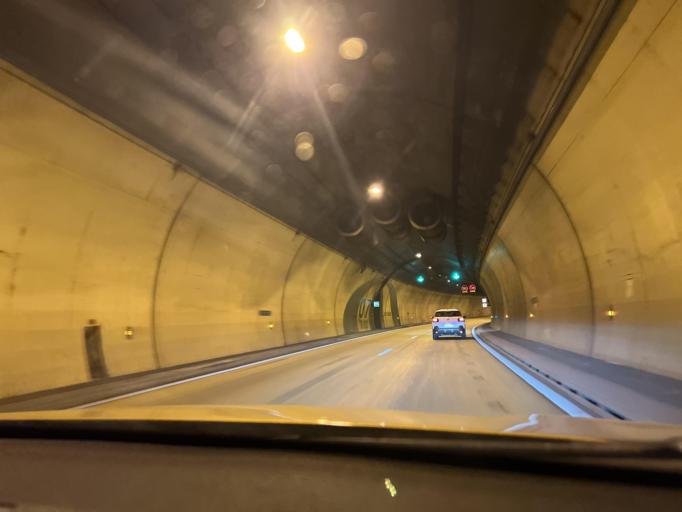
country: FR
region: Provence-Alpes-Cote d'Azur
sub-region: Departement des Alpes-Maritimes
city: Falicon
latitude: 43.7337
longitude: 7.2540
